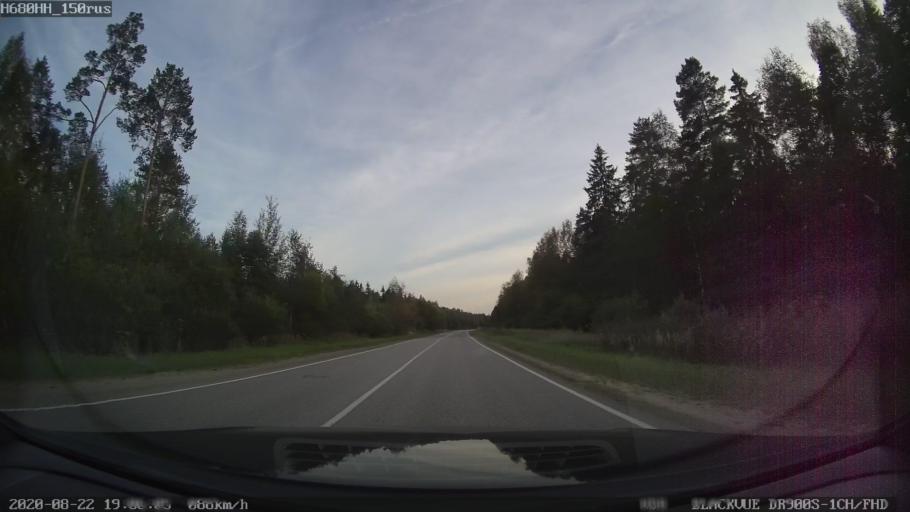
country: RU
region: Tverskaya
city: Sakharovo
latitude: 57.0681
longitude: 36.1085
